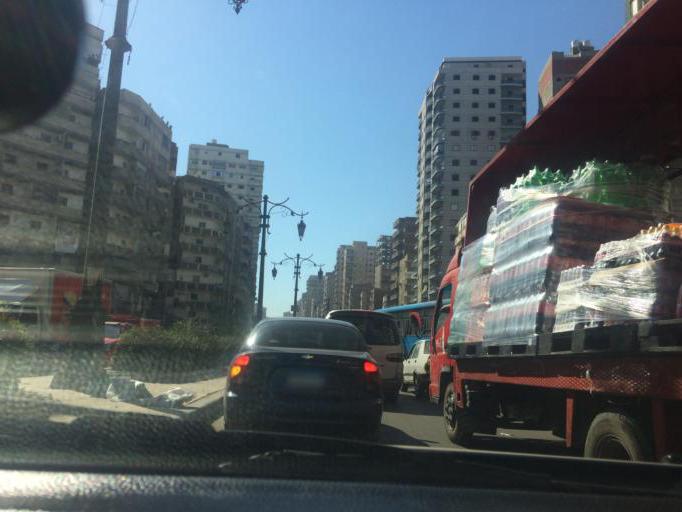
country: EG
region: Alexandria
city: Alexandria
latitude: 31.2608
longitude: 30.0108
